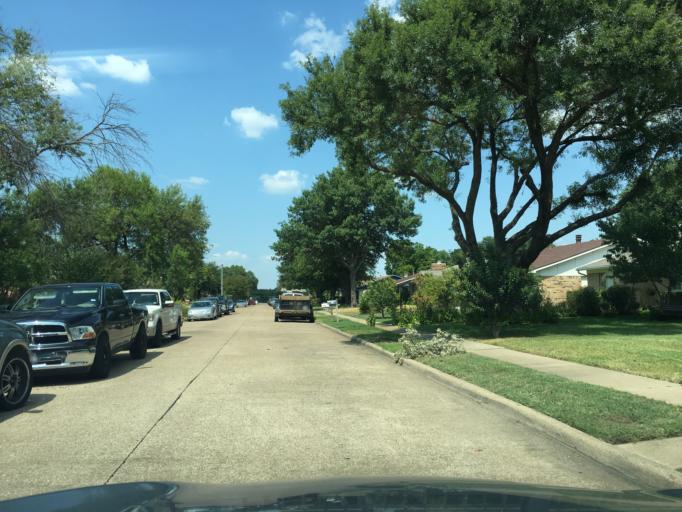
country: US
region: Texas
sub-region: Dallas County
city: Garland
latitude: 32.9483
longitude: -96.6608
